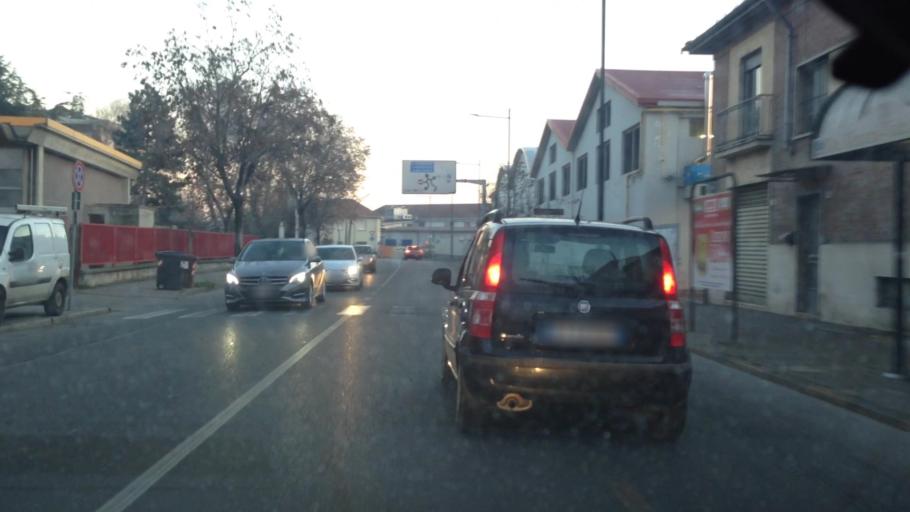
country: IT
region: Piedmont
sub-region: Provincia di Asti
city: Asti
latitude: 44.8947
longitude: 8.1965
